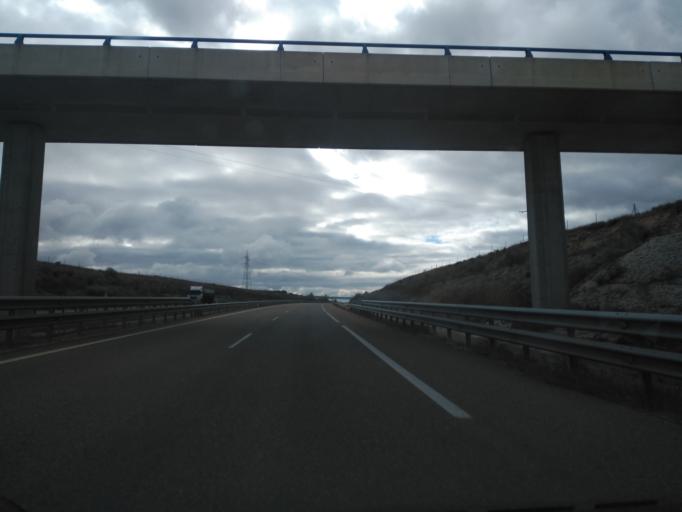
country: ES
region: Castille and Leon
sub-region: Provincia de Palencia
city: Monzon de Campos
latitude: 42.0990
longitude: -4.4821
